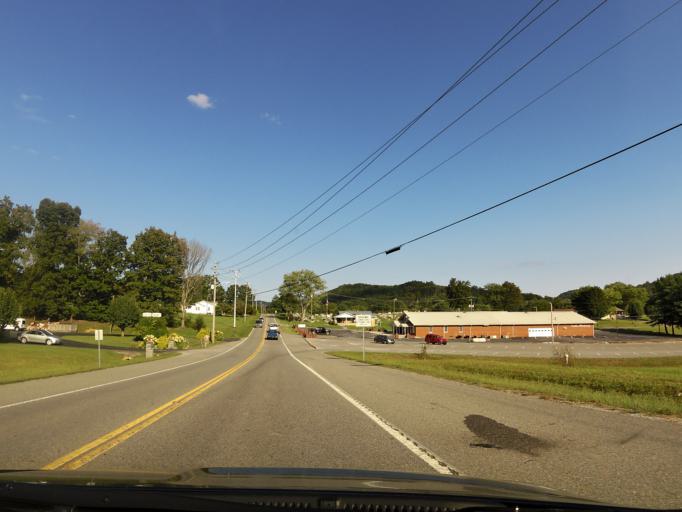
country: US
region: Tennessee
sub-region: Union County
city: Maynardville
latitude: 36.2619
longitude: -83.7775
